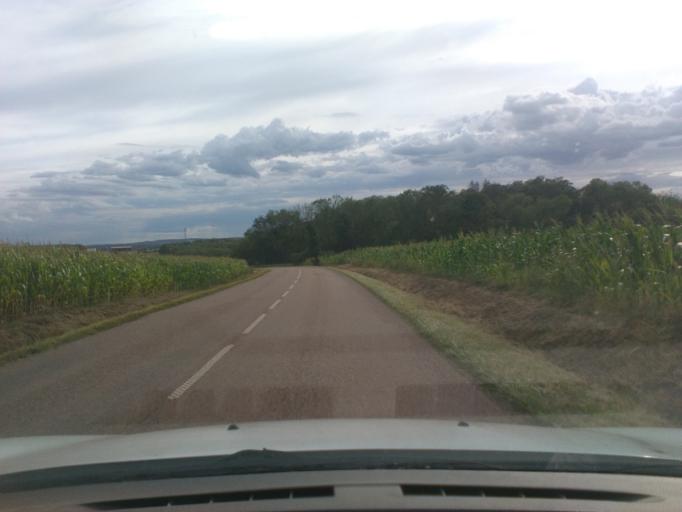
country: FR
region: Lorraine
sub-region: Departement des Vosges
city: Chatel-sur-Moselle
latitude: 48.3323
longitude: 6.4160
